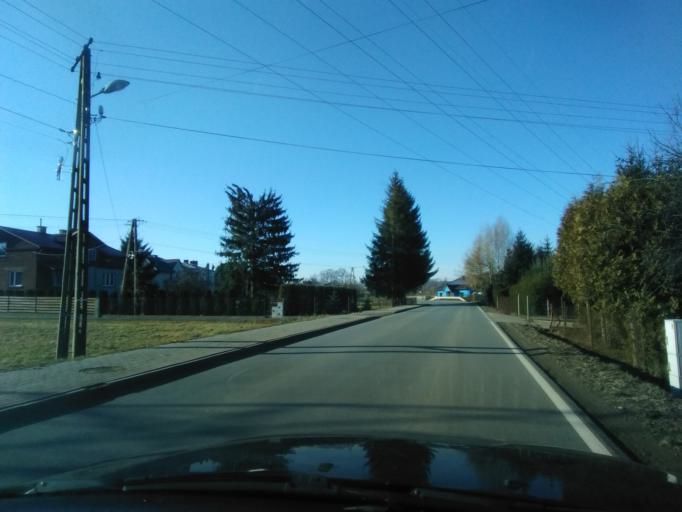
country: PL
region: Subcarpathian Voivodeship
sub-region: Powiat krosnienski
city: Kroscienko Wyzne
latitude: 49.6773
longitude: 21.8567
